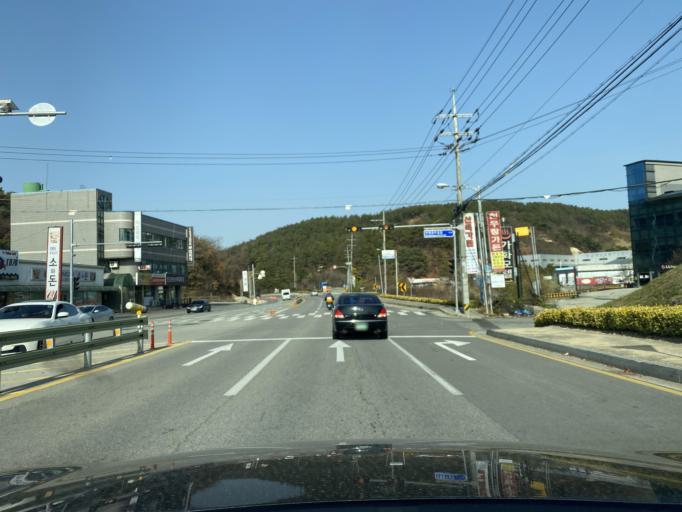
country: KR
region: Chungcheongnam-do
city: Yesan
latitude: 36.6887
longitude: 126.8425
